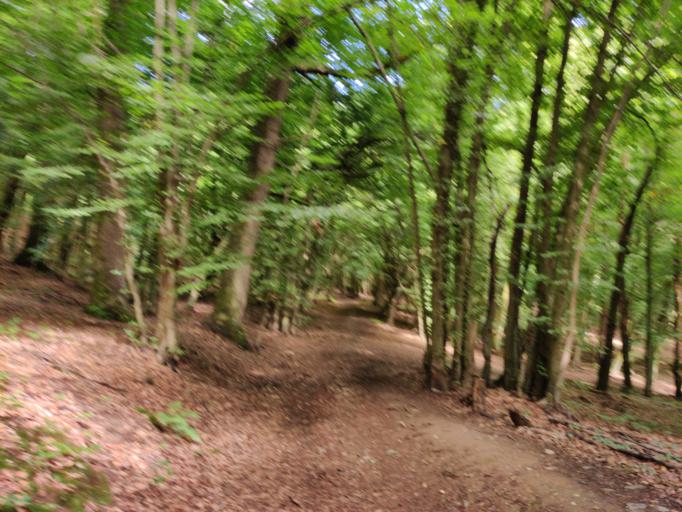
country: AT
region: Carinthia
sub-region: Klagenfurt am Woerthersee
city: Klagenfurt am Woerthersee
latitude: 46.6270
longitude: 14.2657
